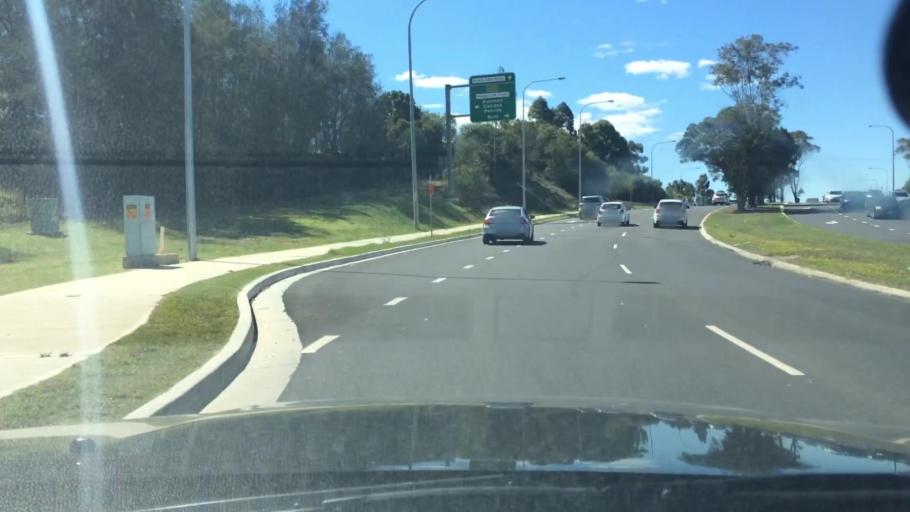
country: AU
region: New South Wales
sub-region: Campbelltown Municipality
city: Campbelltown
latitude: -34.0694
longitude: 150.8004
